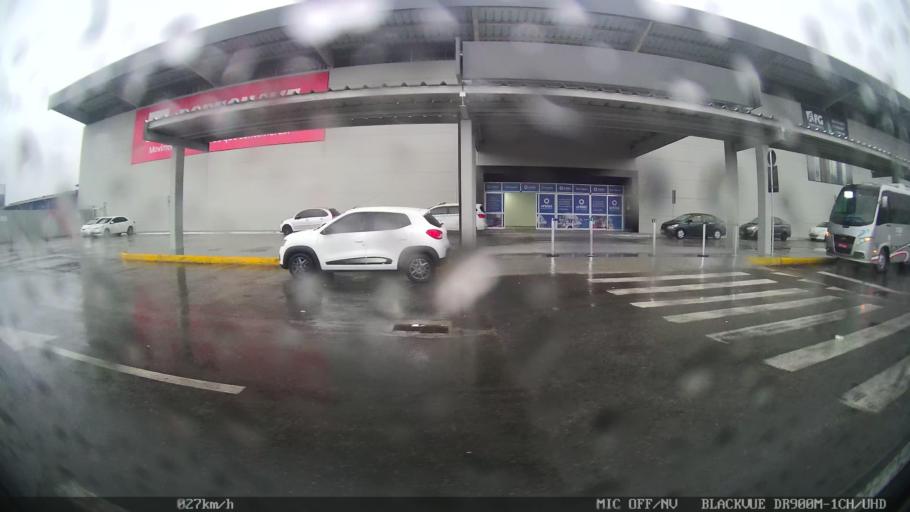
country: BR
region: Santa Catarina
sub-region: Navegantes
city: Navegantes
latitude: -26.8811
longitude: -48.6492
